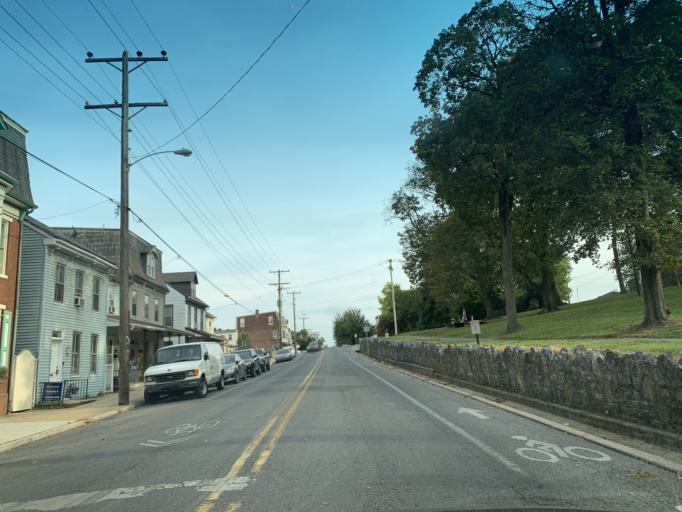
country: US
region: Pennsylvania
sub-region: York County
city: York
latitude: 39.9660
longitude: -76.7386
